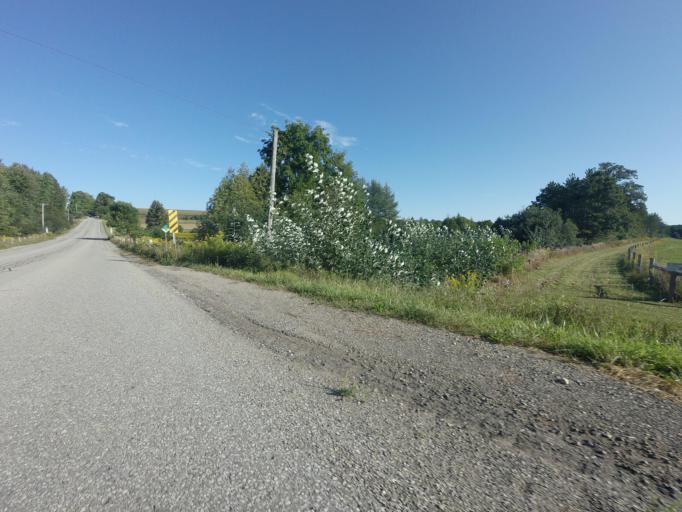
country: CA
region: Ontario
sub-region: Wellington County
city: Guelph
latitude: 43.6510
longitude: -80.4161
